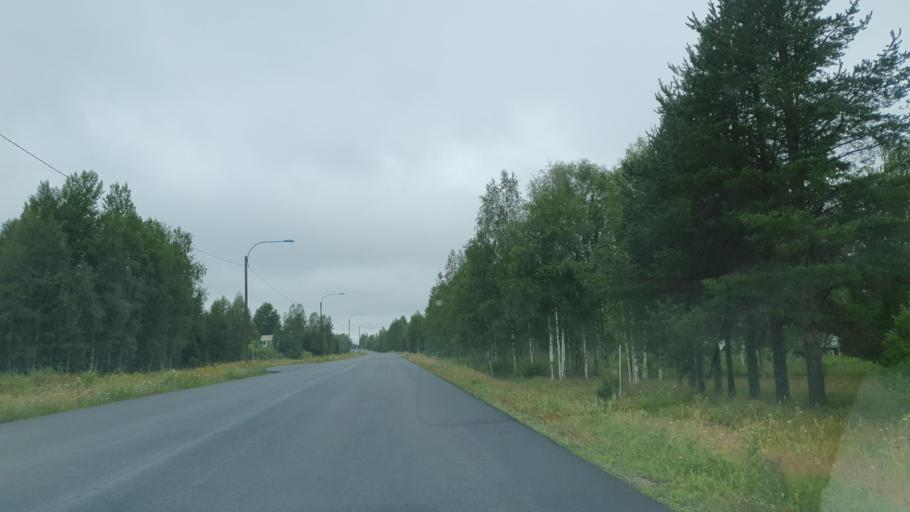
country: FI
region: Lapland
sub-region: Itae-Lappi
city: Pelkosenniemi
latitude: 67.1160
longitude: 27.5044
